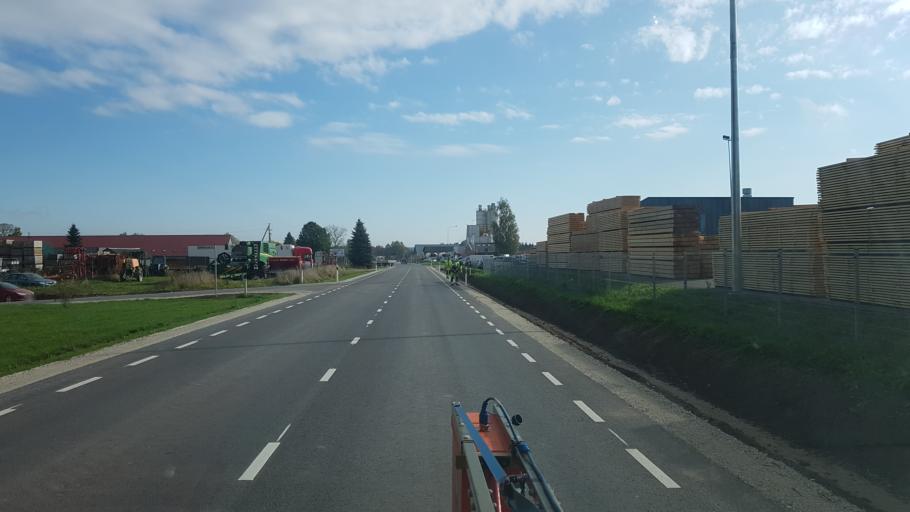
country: EE
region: Tartu
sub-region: UElenurme vald
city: Ulenurme
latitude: 58.2937
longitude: 26.7063
